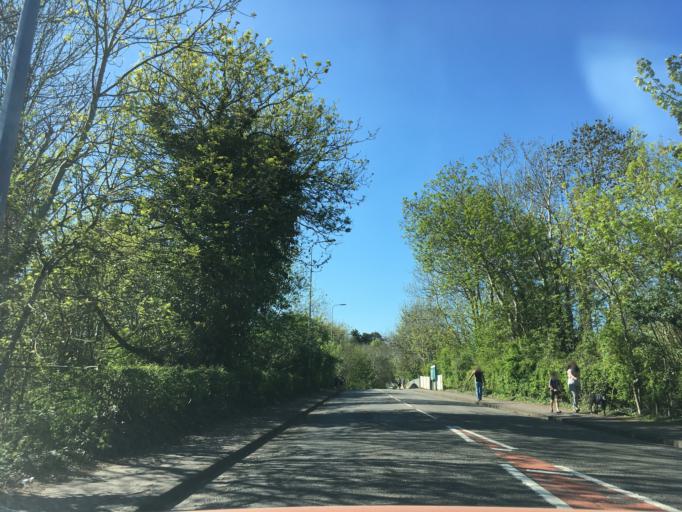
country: GB
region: Wales
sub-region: Cardiff
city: Radyr
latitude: 51.5198
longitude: -3.2314
